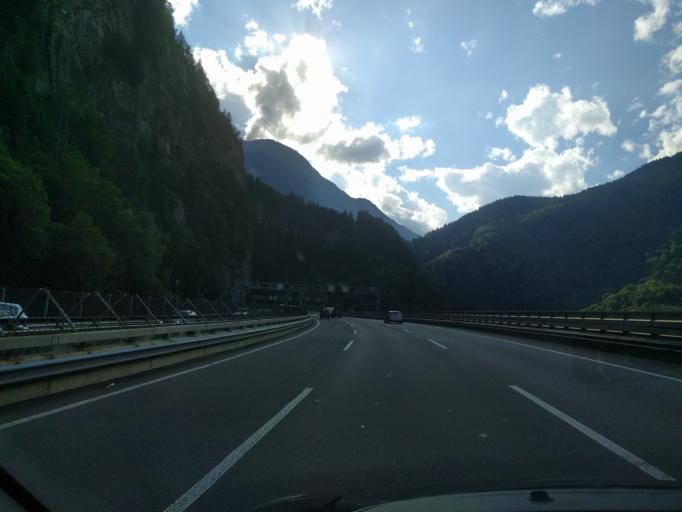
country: CH
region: Ticino
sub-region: Leventina District
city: Faido
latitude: 46.4888
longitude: 8.7643
